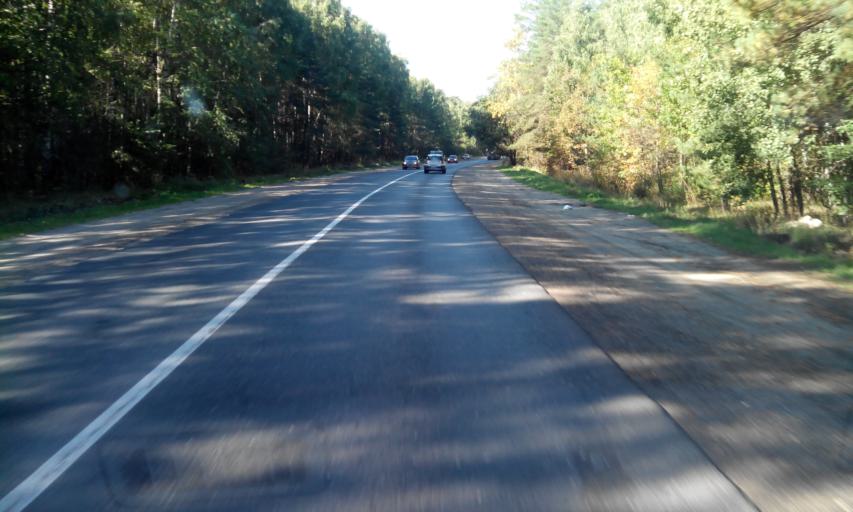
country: RU
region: Penza
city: Zarechnyy
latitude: 53.2141
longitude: 45.1422
